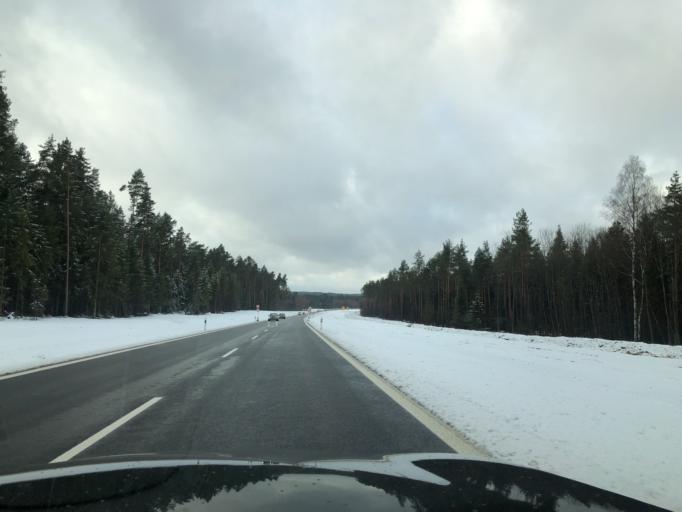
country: DE
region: Bavaria
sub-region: Upper Palatinate
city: Breitenbrunn
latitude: 49.3872
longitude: 11.9986
